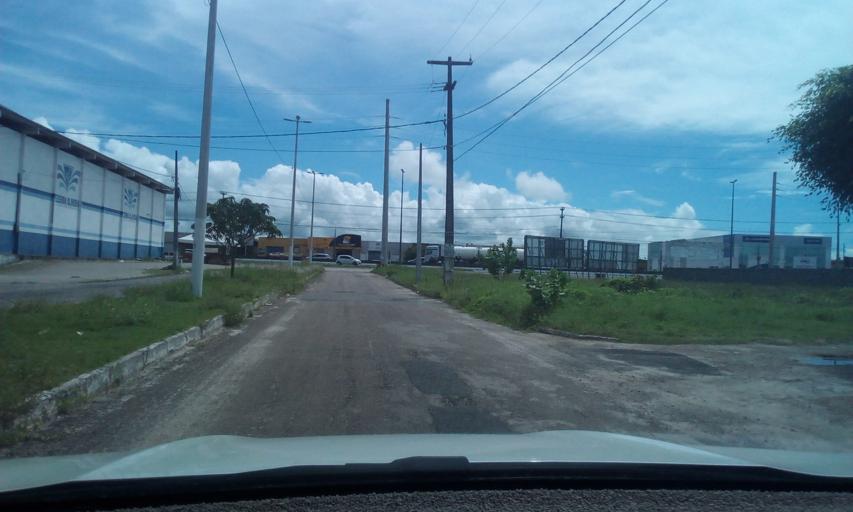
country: BR
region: Paraiba
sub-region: Joao Pessoa
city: Joao Pessoa
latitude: -7.0515
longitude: -34.8488
